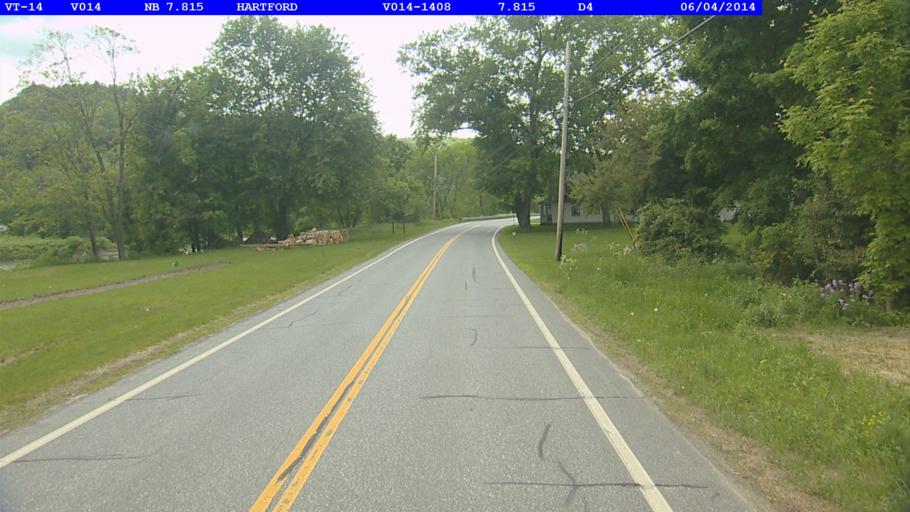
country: US
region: Vermont
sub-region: Windsor County
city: Wilder
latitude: 43.7226
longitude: -72.4251
